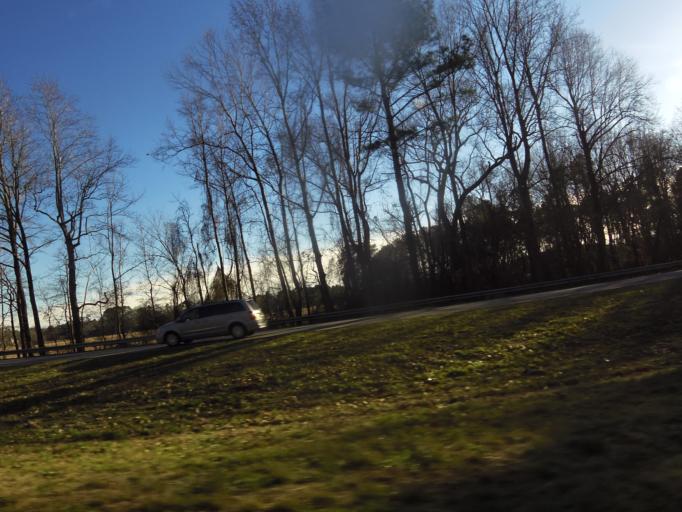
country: US
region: Virginia
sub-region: City of Suffolk
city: Suffolk
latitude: 36.7651
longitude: -76.5662
